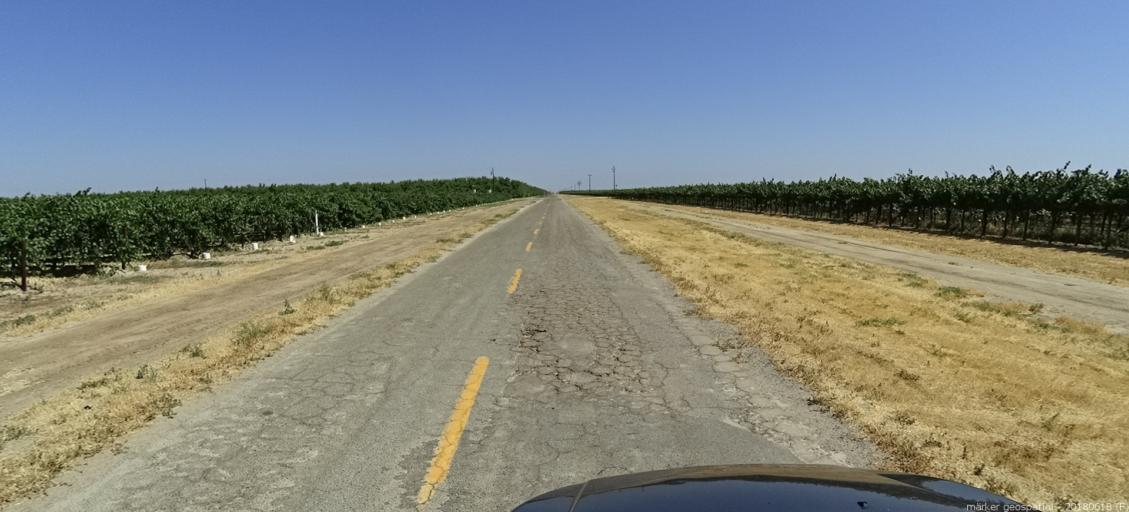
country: US
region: California
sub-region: Madera County
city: Parkwood
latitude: 36.8422
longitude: -120.1828
